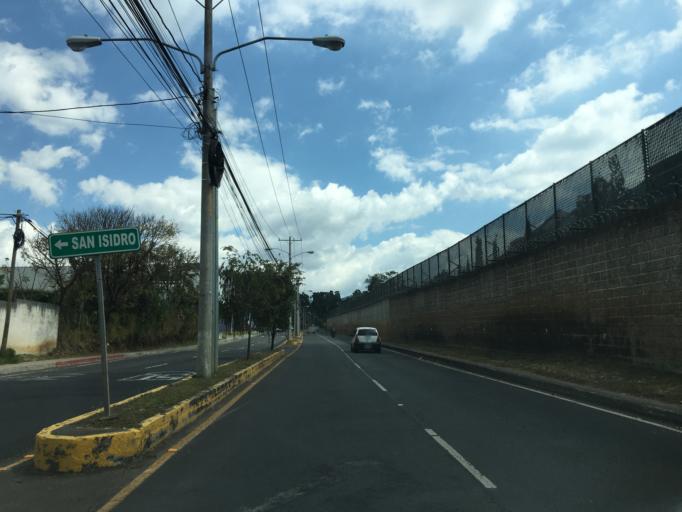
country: GT
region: Guatemala
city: Santa Catarina Pinula
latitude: 14.6070
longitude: -90.4699
